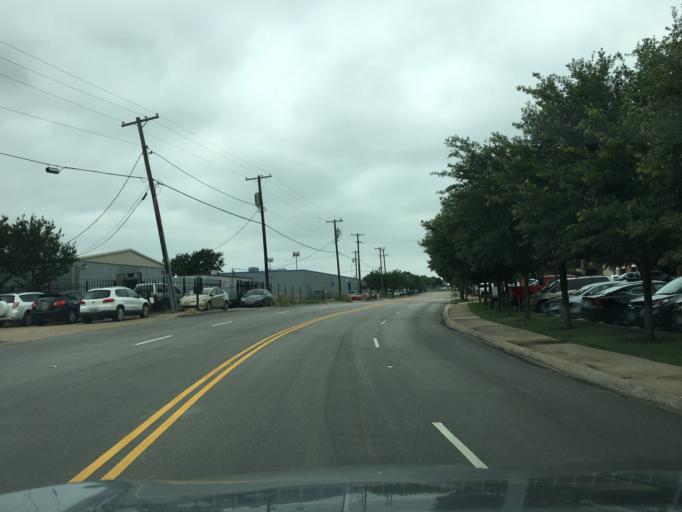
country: US
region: Texas
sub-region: Dallas County
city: Richardson
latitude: 32.9339
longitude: -96.7444
